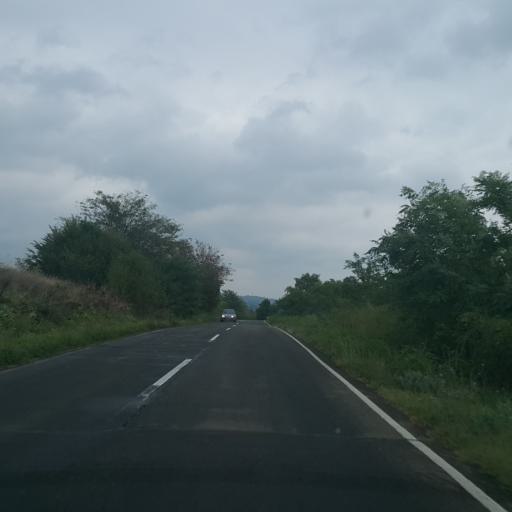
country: RS
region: Central Serbia
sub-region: Nisavski Okrug
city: Aleksinac
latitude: 43.5838
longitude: 21.6558
